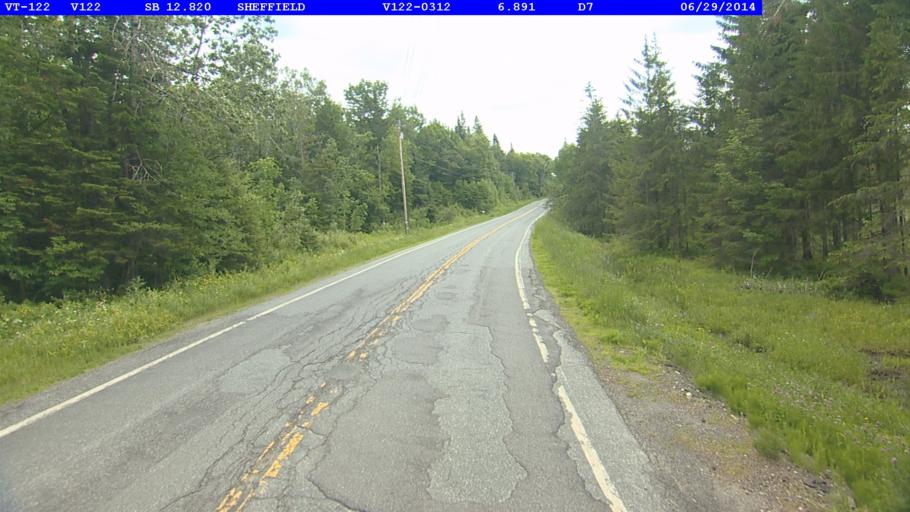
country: US
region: Vermont
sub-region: Caledonia County
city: Lyndonville
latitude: 44.6674
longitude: -72.1609
